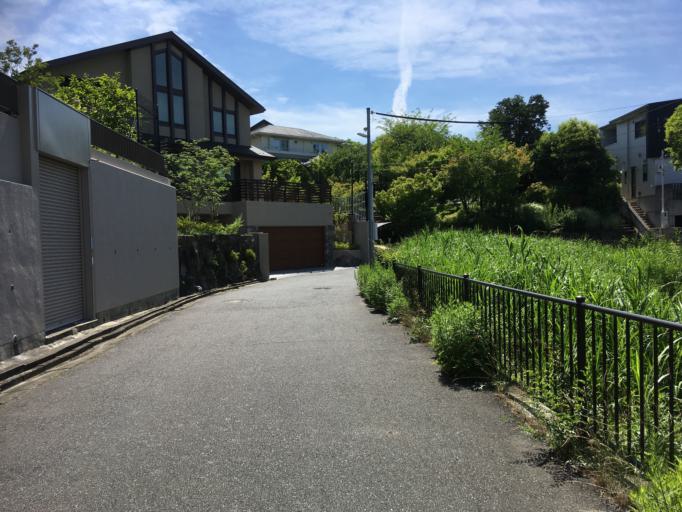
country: JP
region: Nara
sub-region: Ikoma-shi
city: Ikoma
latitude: 34.7085
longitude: 135.7479
